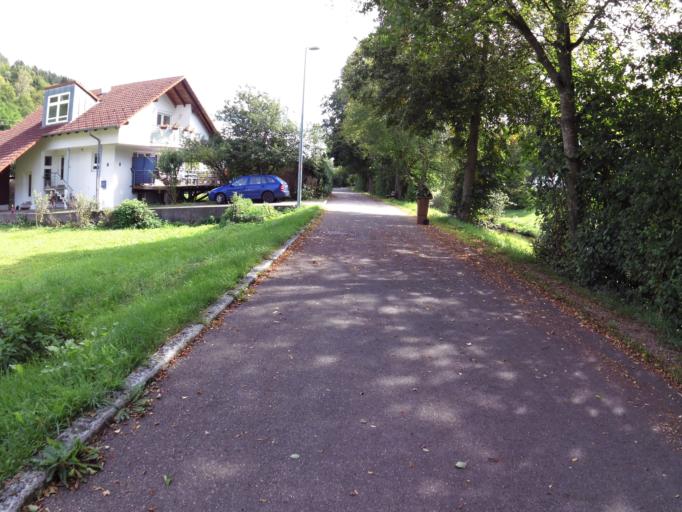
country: DE
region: Baden-Wuerttemberg
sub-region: Freiburg Region
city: Oberndorf
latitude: 48.3112
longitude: 8.5717
